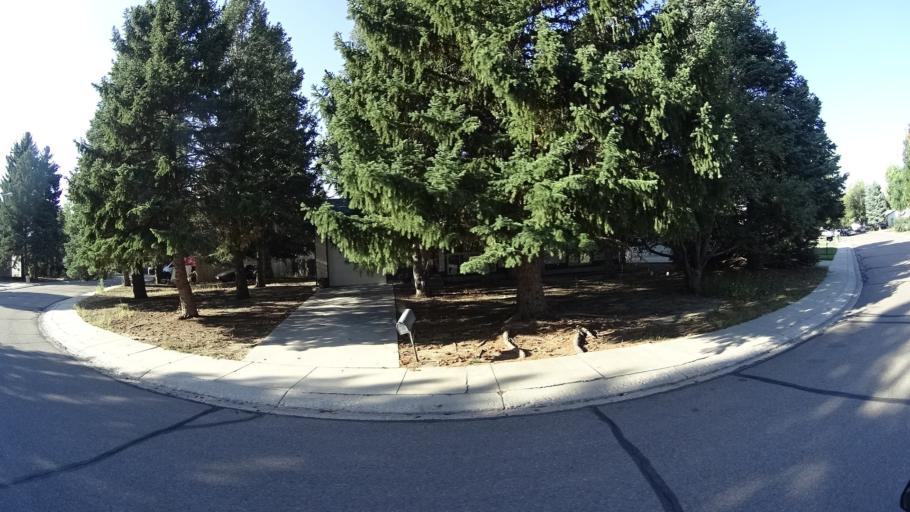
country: US
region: Colorado
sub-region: El Paso County
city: Cimarron Hills
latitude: 38.8894
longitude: -104.7445
